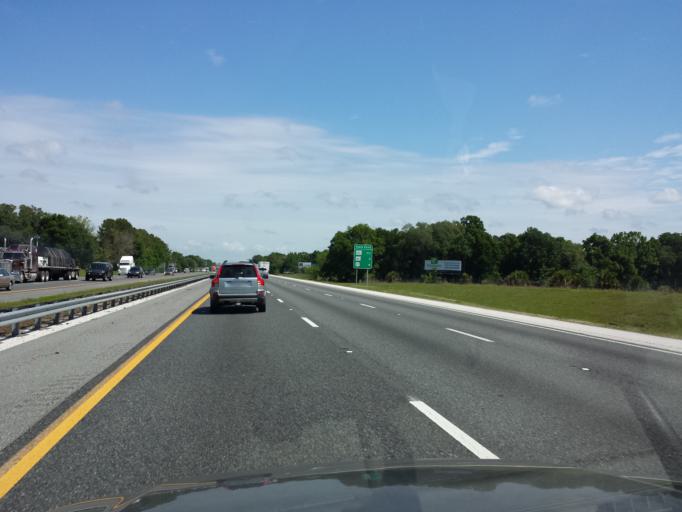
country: US
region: Florida
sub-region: Marion County
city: Ocala
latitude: 29.1224
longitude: -82.1848
